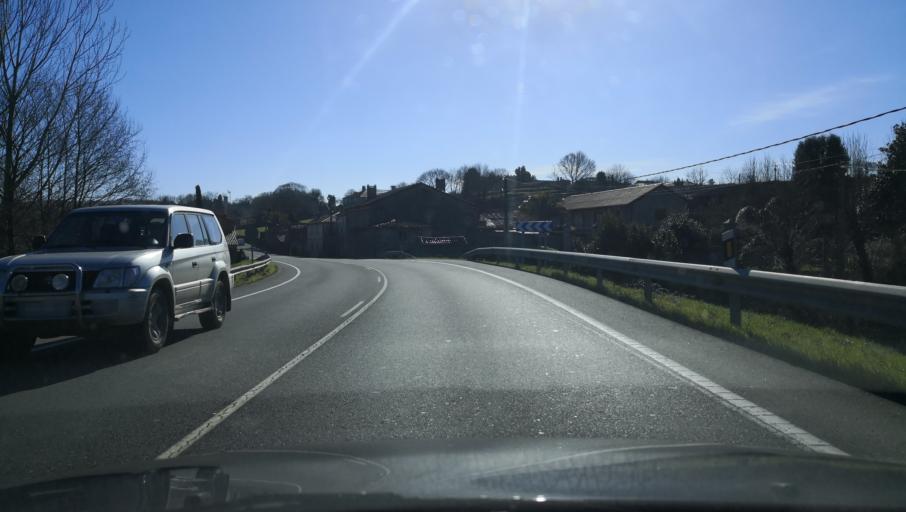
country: ES
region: Galicia
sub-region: Provincia de Pontevedra
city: Silleda
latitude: 42.7240
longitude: -8.2963
